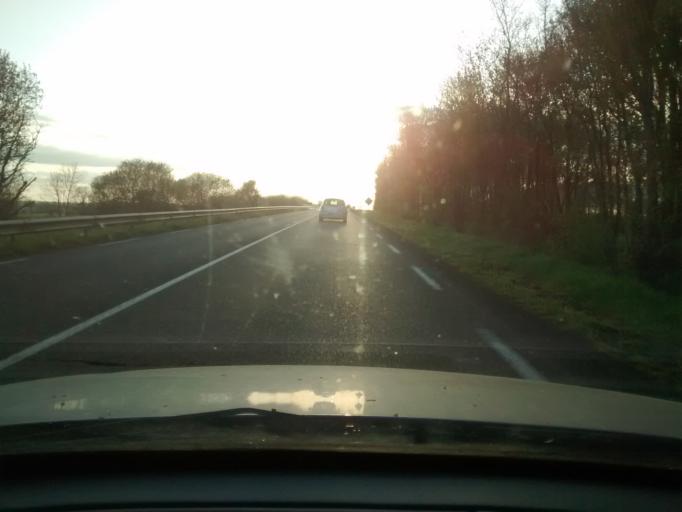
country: FR
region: Pays de la Loire
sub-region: Departement de la Mayenne
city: Sainte-Suzanne
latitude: 48.0332
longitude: -0.3543
